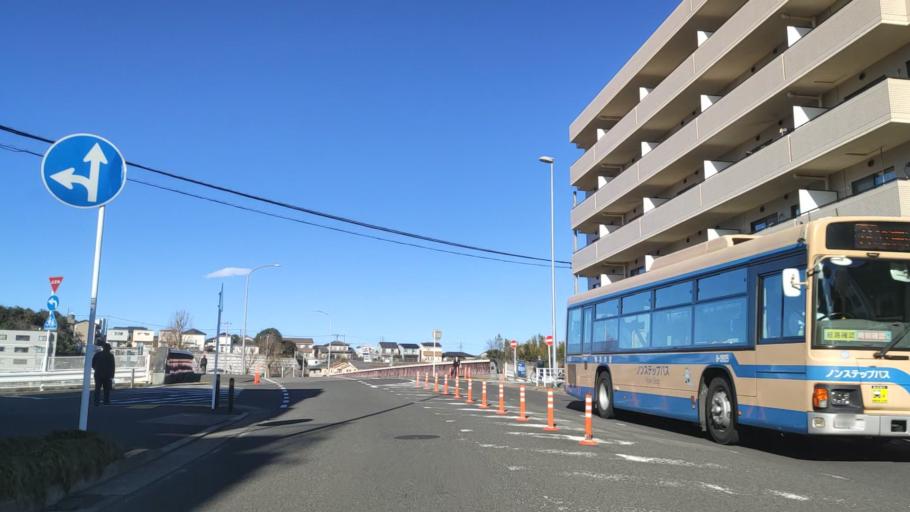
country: JP
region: Tokyo
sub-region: Machida-shi
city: Machida
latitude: 35.5167
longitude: 139.5414
